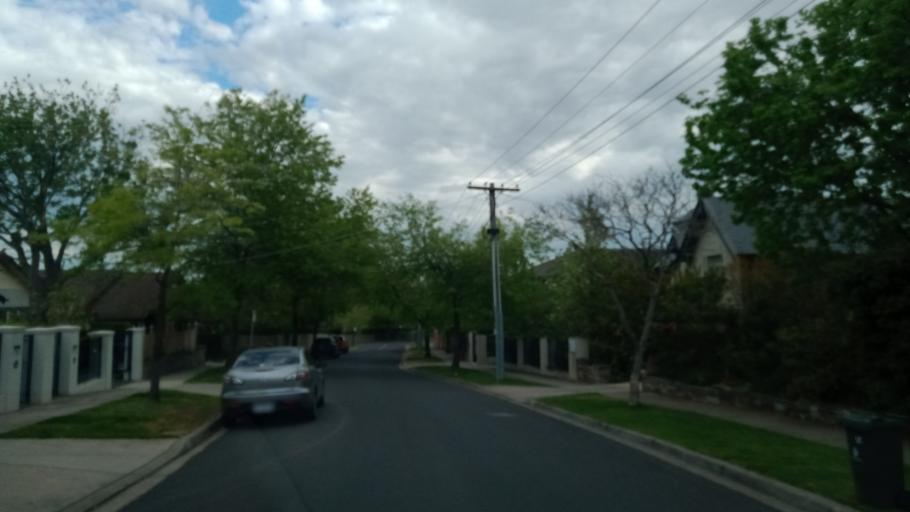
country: AU
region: Victoria
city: Glenferrie
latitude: -37.8429
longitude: 145.0512
